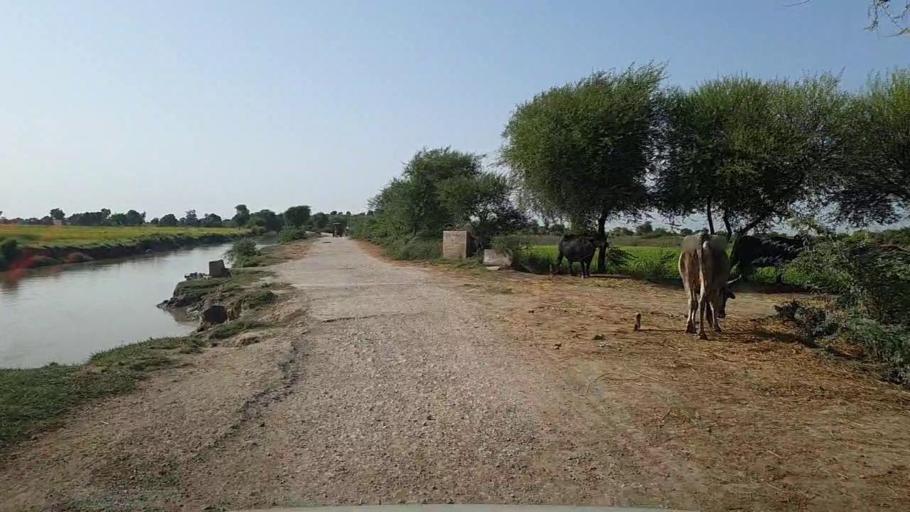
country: PK
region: Sindh
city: Kario
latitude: 24.8034
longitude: 68.5507
